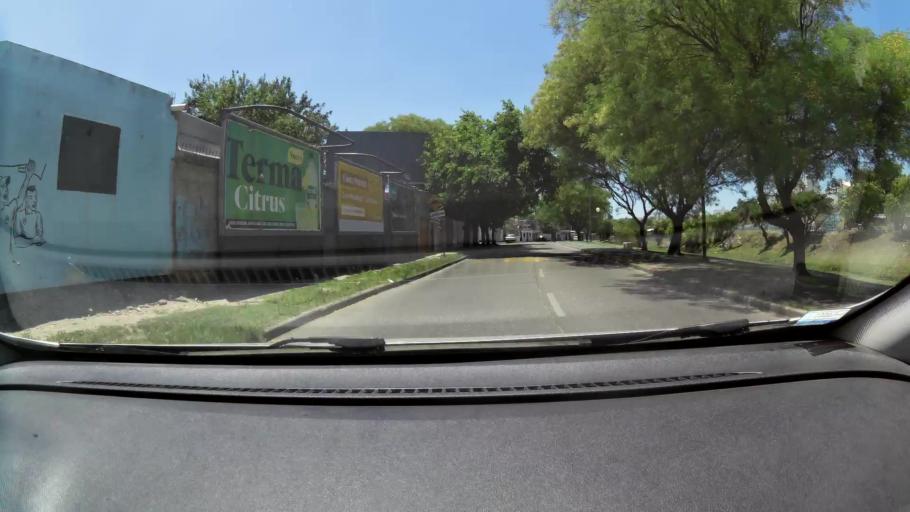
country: AR
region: Cordoba
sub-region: Departamento de Capital
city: Cordoba
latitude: -31.3992
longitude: -64.2043
